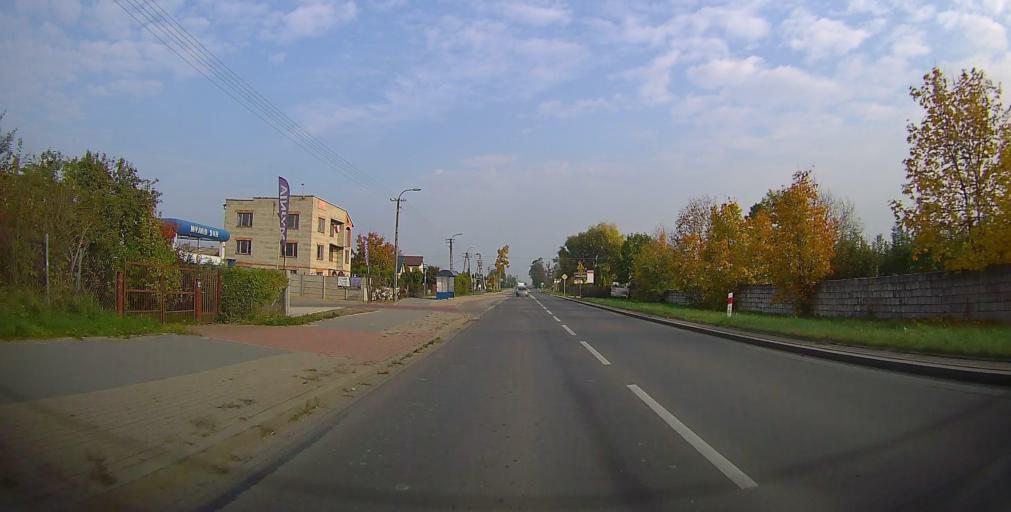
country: PL
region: Masovian Voivodeship
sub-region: Powiat grojecki
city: Mogielnica
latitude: 51.7048
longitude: 20.7365
